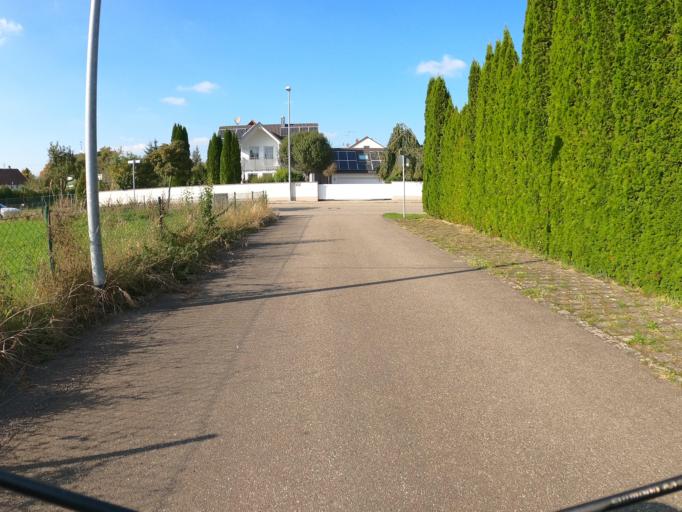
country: DE
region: Bavaria
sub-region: Swabia
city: Leipheim
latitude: 48.4460
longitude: 10.2288
